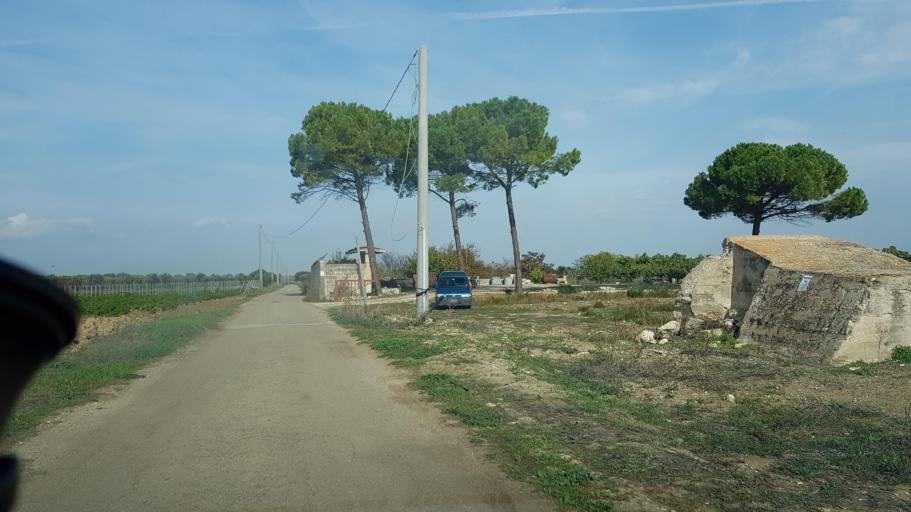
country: IT
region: Apulia
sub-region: Provincia di Brindisi
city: San Pancrazio Salentino
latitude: 40.4267
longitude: 17.8596
